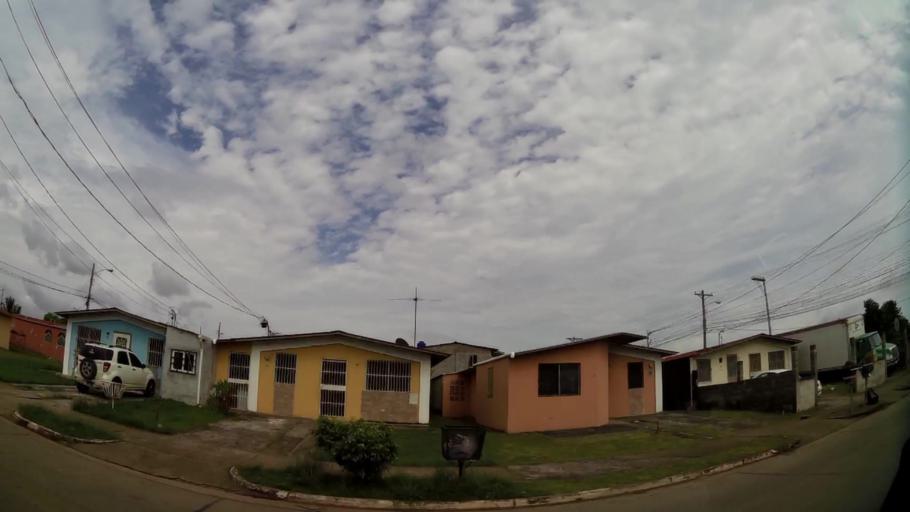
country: PA
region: Panama
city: Tocumen
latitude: 9.0469
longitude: -79.4119
